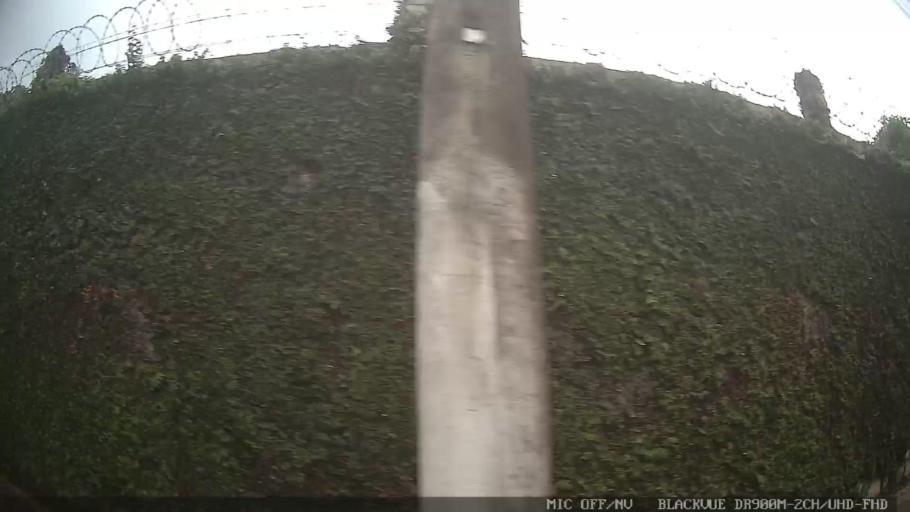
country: BR
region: Sao Paulo
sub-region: Mogi das Cruzes
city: Mogi das Cruzes
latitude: -23.5242
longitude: -46.1641
